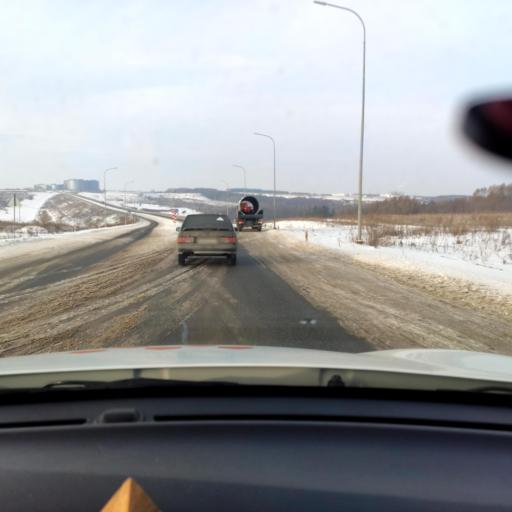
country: RU
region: Tatarstan
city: Sviyazhsk
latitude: 55.7427
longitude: 48.7749
